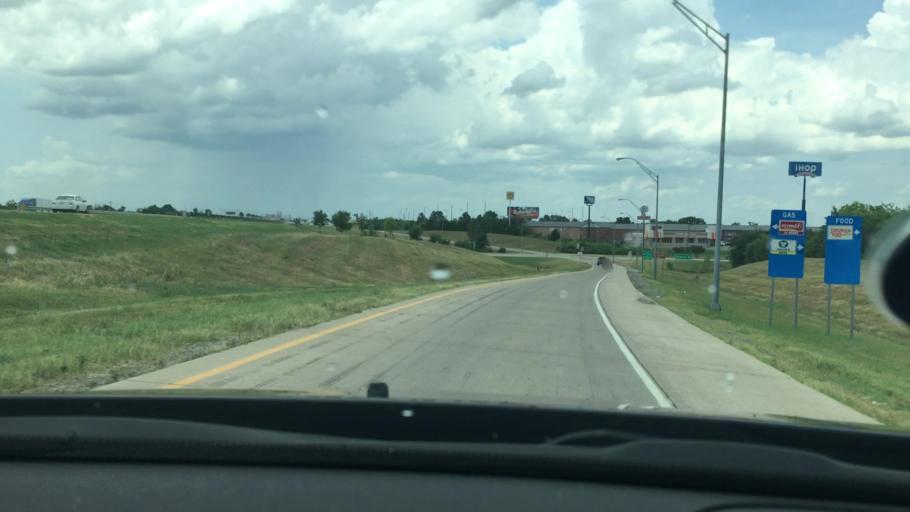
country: US
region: Oklahoma
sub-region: Carter County
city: Ardmore
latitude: 34.1996
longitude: -97.1635
